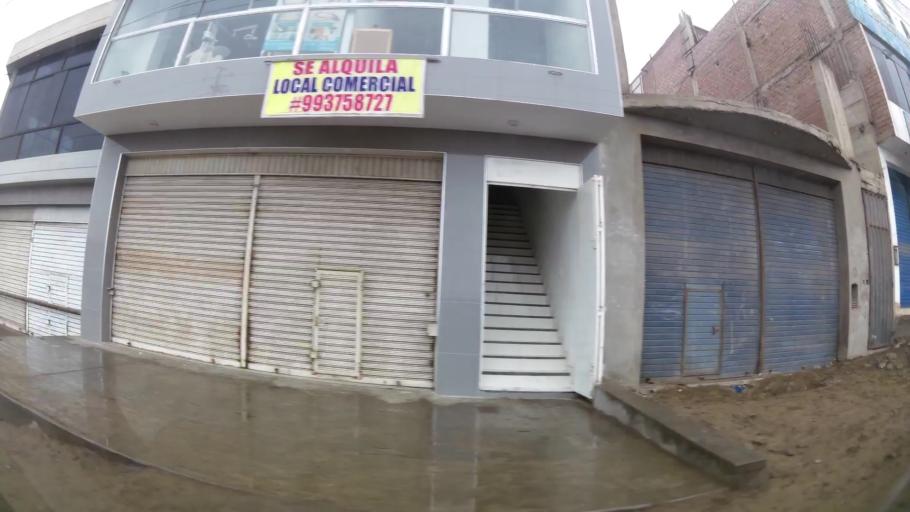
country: PE
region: Lima
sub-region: Lima
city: Santa Rosa
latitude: -11.8316
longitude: -77.1478
